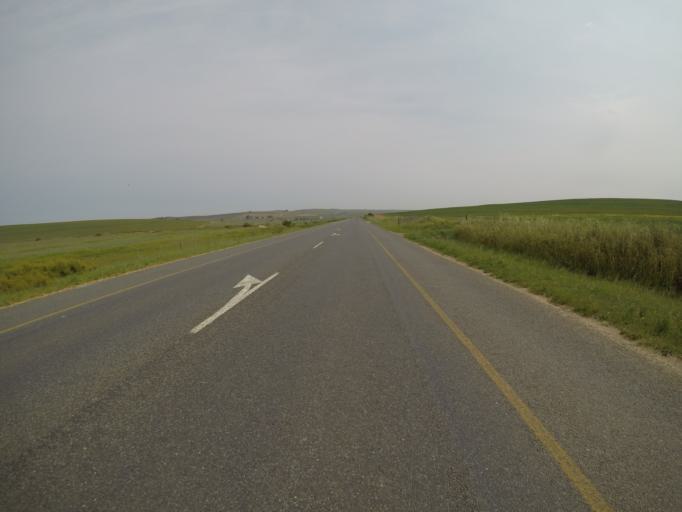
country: ZA
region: Western Cape
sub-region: West Coast District Municipality
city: Malmesbury
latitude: -33.4504
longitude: 18.7735
